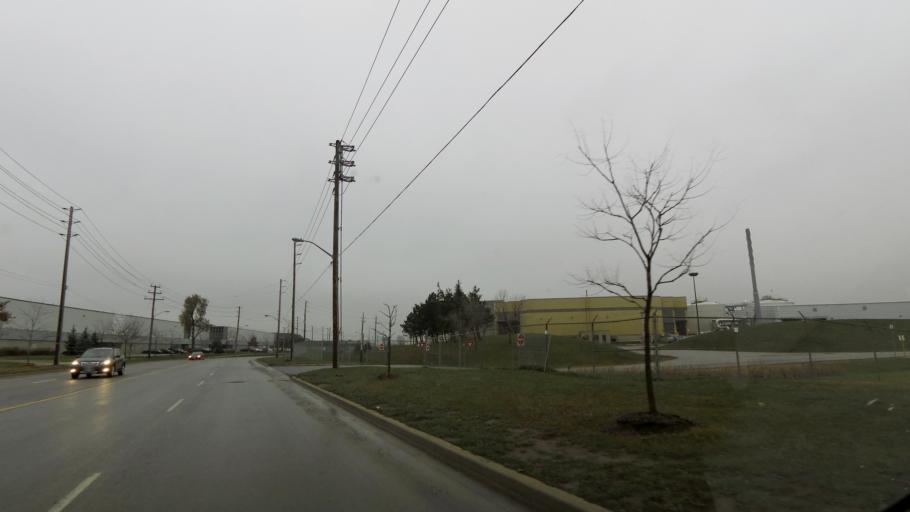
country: CA
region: Ontario
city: Etobicoke
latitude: 43.7025
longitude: -79.6024
